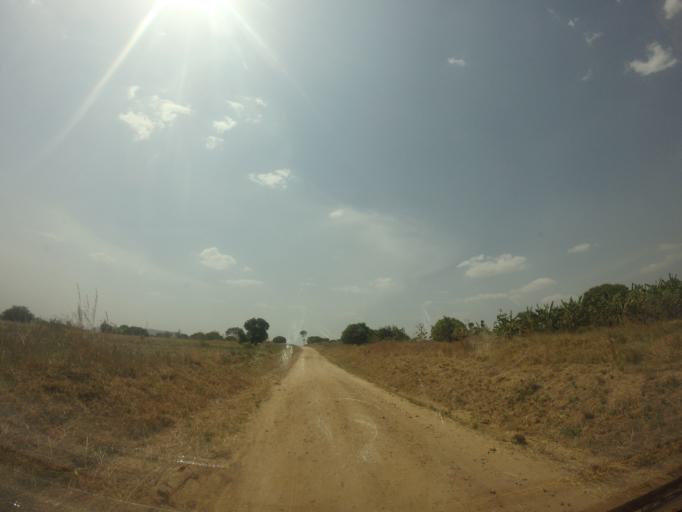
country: UG
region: Northern Region
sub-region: Arua District
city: Arua
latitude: 2.9121
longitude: 31.0479
